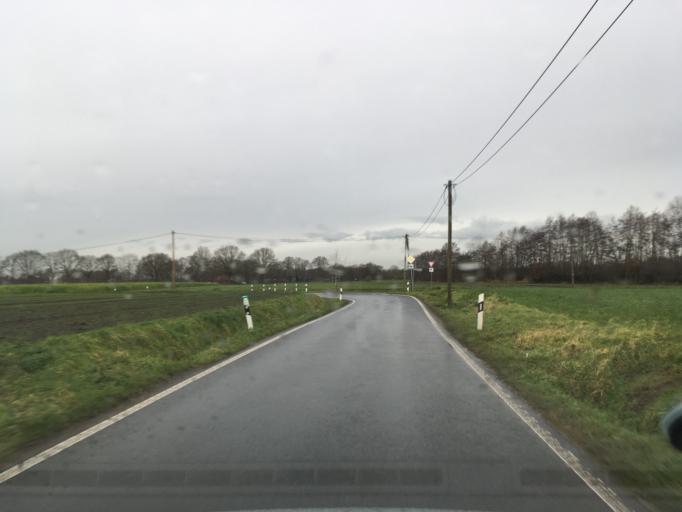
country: DE
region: North Rhine-Westphalia
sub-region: Regierungsbezirk Munster
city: Heek
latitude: 52.1381
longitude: 7.1151
